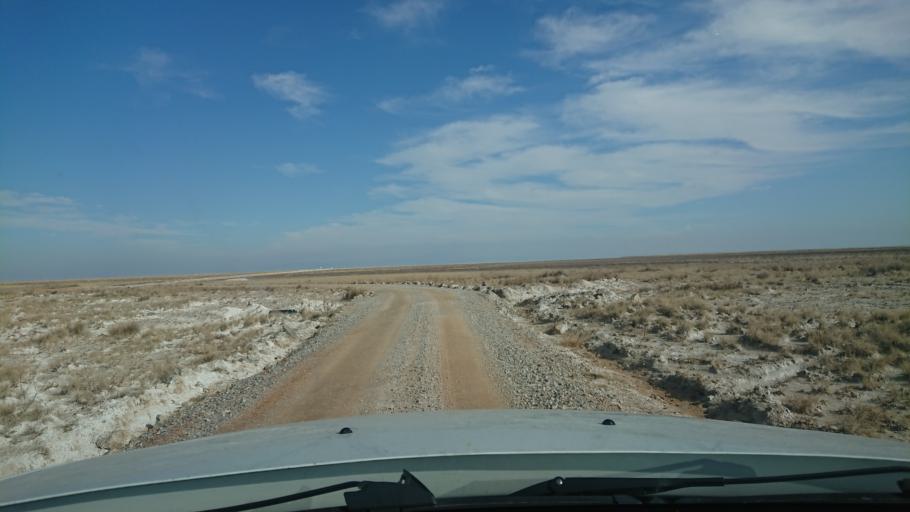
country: TR
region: Aksaray
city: Eskil
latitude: 38.4811
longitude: 33.4701
